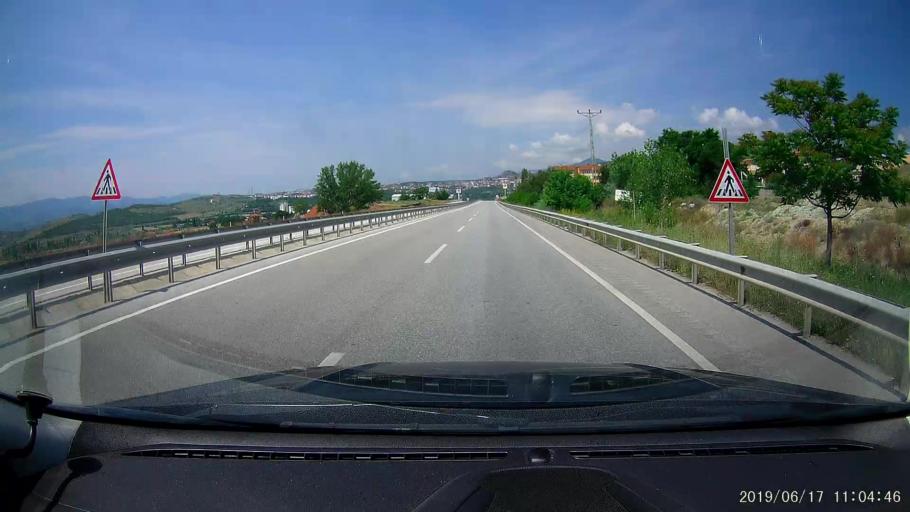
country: TR
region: Kastamonu
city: Tosya
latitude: 41.0193
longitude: 34.0874
